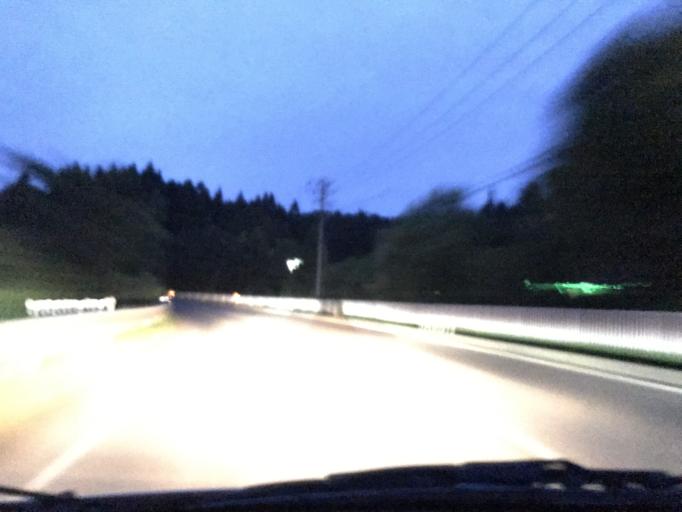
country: JP
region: Iwate
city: Kitakami
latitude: 39.2941
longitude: 141.1676
